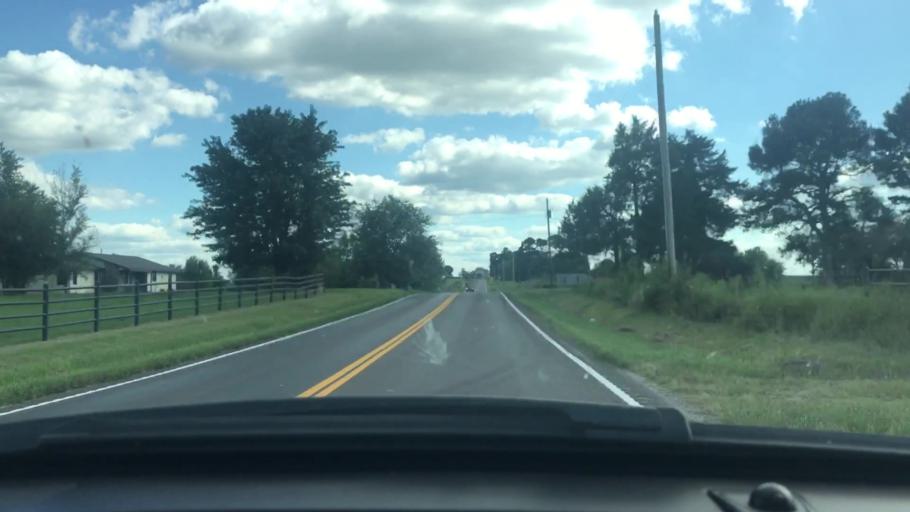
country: US
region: Missouri
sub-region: Wright County
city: Mountain Grove
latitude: 37.1719
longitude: -92.2671
